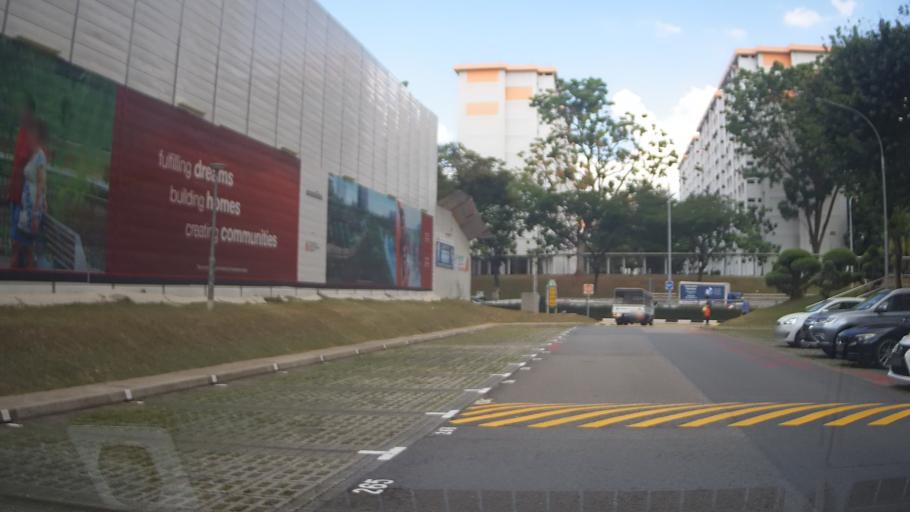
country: SG
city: Singapore
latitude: 1.3212
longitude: 103.7632
